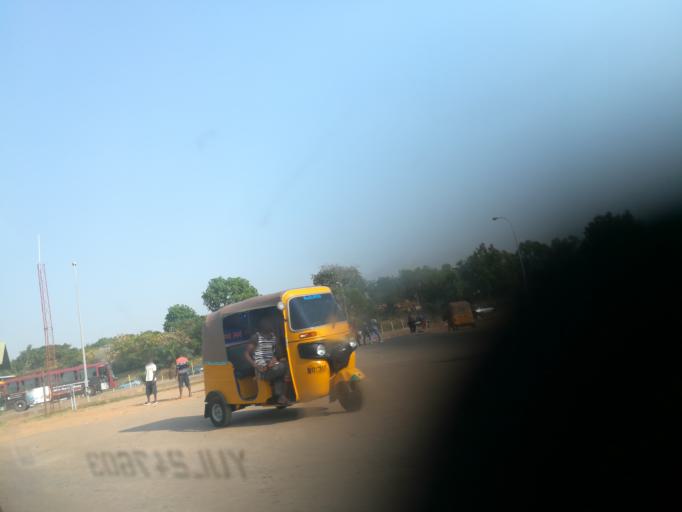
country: NG
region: Abuja Federal Capital Territory
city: Abuja
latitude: 9.0539
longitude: 7.4530
